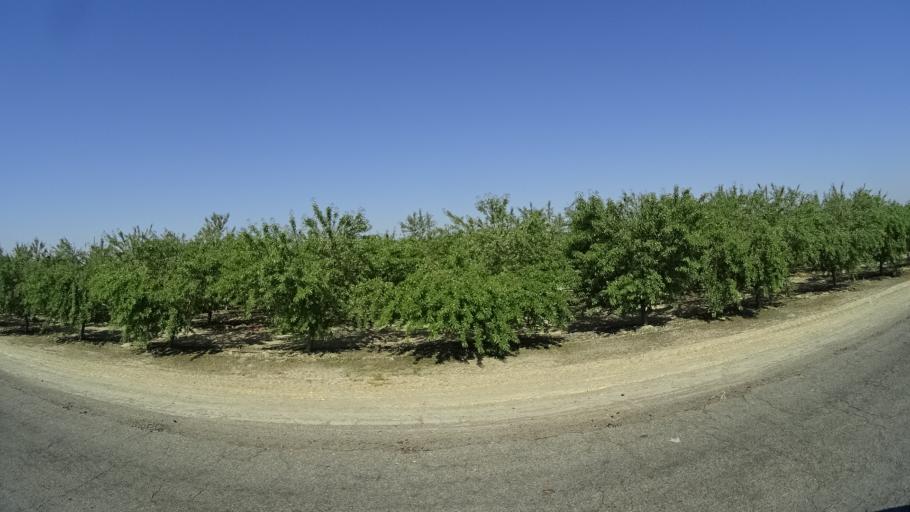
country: US
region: California
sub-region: Fresno County
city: Kingsburg
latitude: 36.3981
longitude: -119.5469
